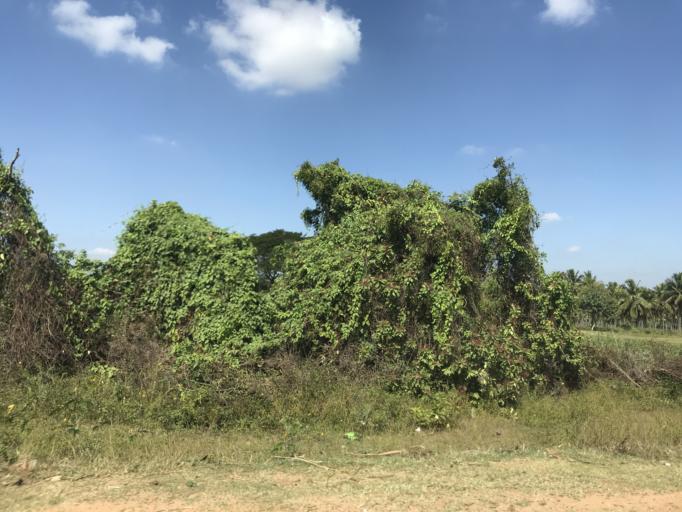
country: IN
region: Karnataka
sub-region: Mysore
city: Hunsur
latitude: 12.3585
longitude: 76.2978
